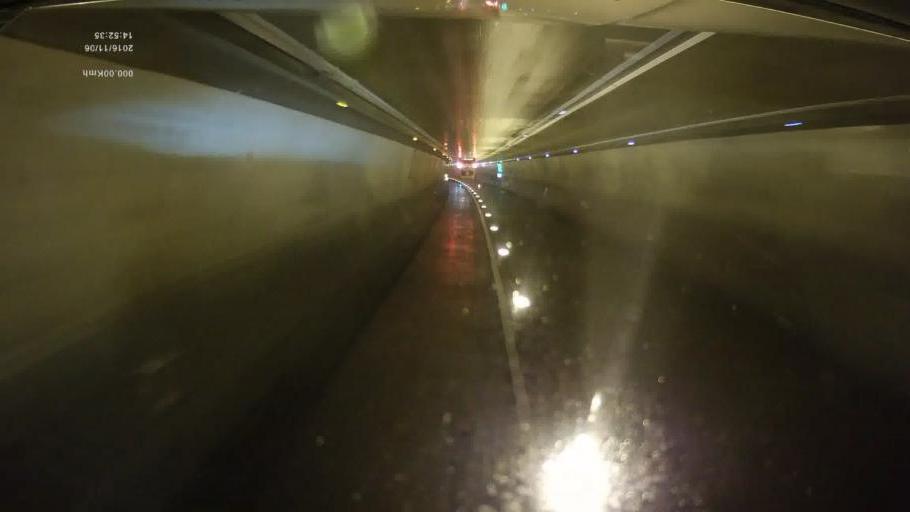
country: SK
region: Presovsky
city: Spisske Podhradie
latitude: 49.0105
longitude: 20.8462
